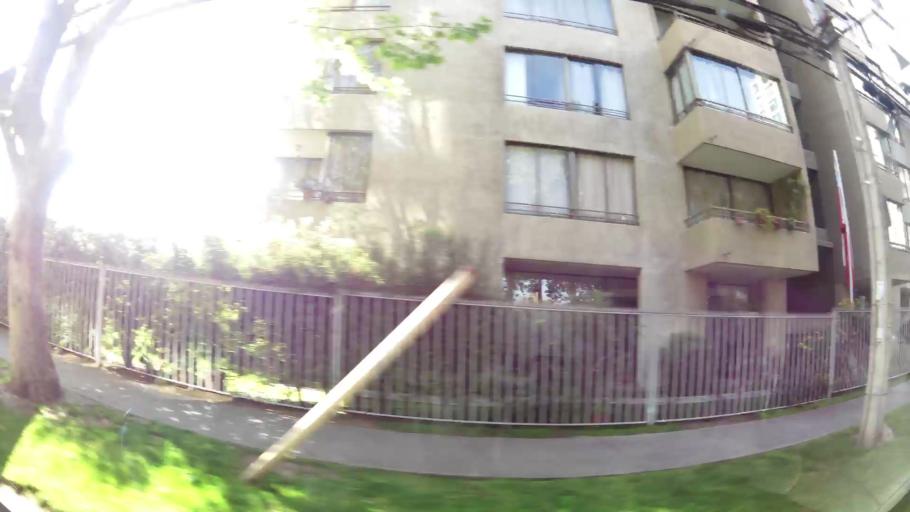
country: CL
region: Santiago Metropolitan
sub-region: Provincia de Santiago
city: Santiago
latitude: -33.5074
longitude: -70.6586
